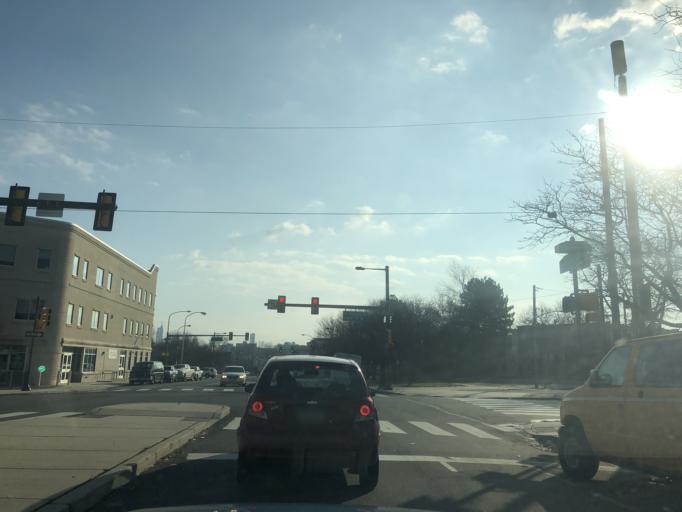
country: US
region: Pennsylvania
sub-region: Delaware County
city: Millbourne
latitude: 39.9654
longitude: -75.2259
